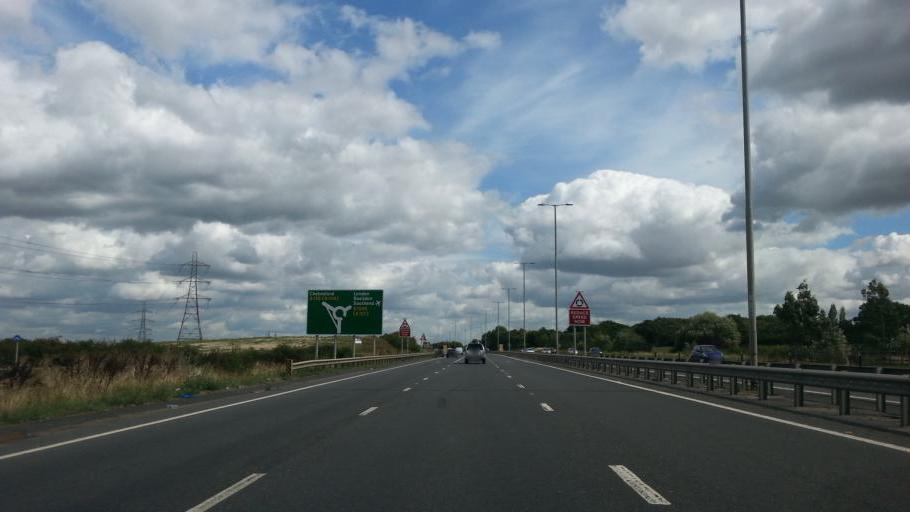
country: GB
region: England
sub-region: Essex
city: South Benfleet
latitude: 51.5797
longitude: 0.5545
